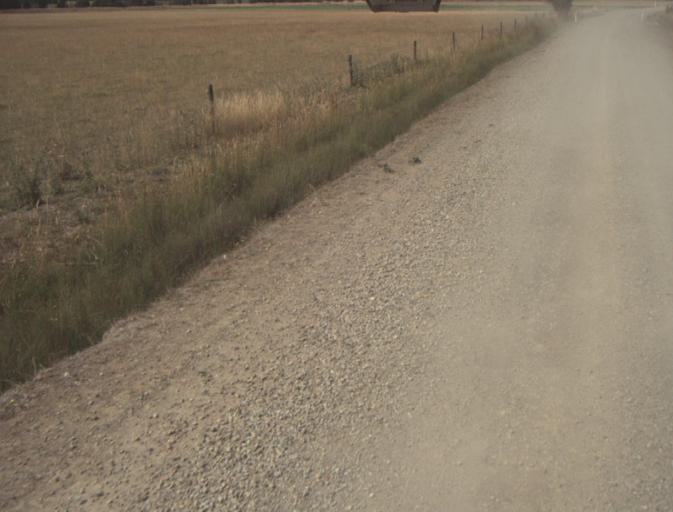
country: AU
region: Tasmania
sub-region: Northern Midlands
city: Evandale
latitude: -41.4772
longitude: 147.4448
